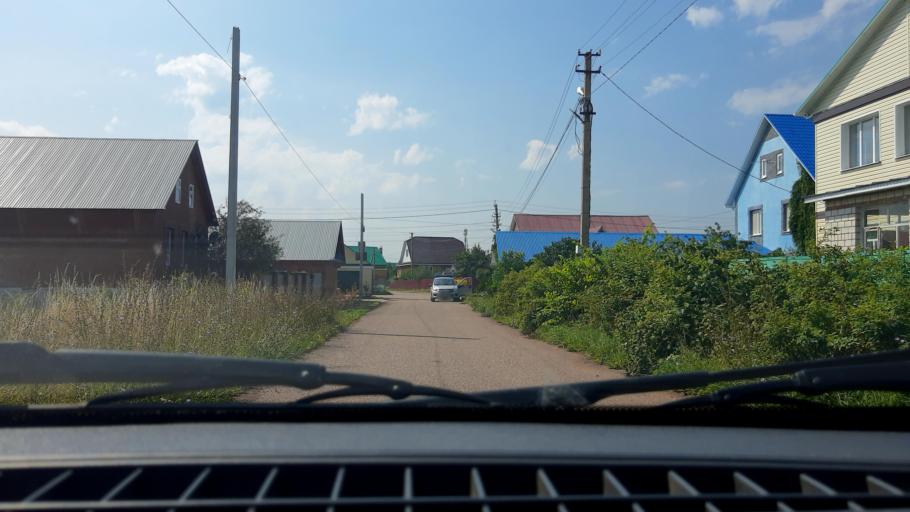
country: RU
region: Bashkortostan
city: Mikhaylovka
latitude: 54.8423
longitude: 55.8294
